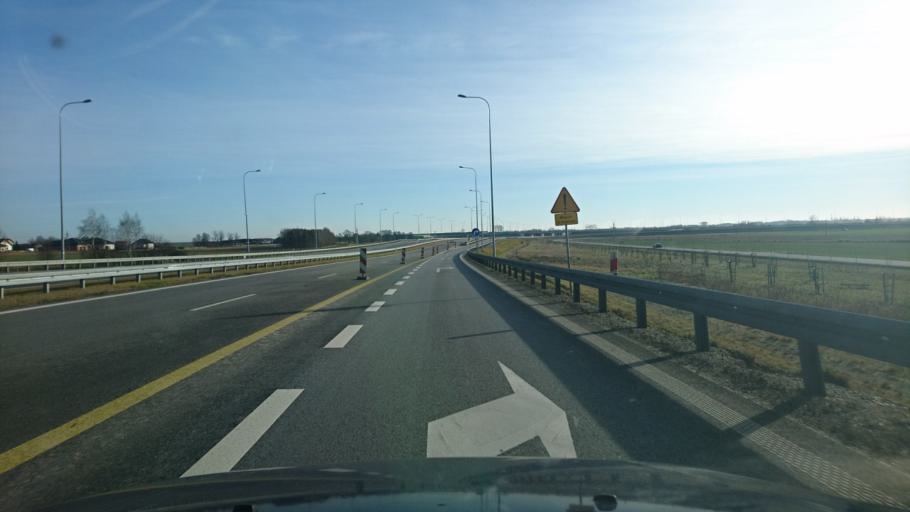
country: PL
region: Greater Poland Voivodeship
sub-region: Powiat kepinski
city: Kepno
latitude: 51.3218
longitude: 18.0013
